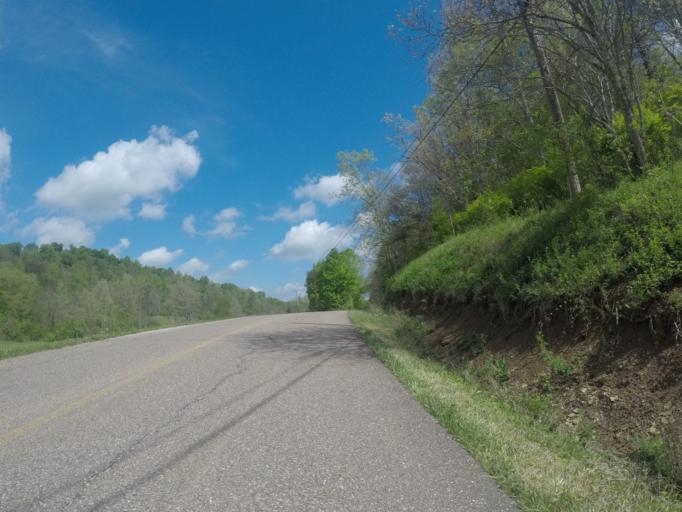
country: US
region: West Virginia
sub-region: Cabell County
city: Huntington
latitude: 38.5138
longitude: -82.4391
